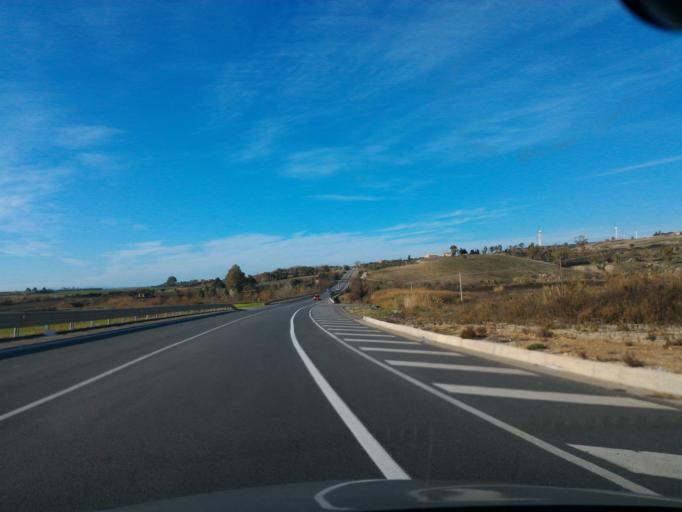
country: IT
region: Calabria
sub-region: Provincia di Crotone
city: Isola di Capo Rizzuto
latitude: 38.9402
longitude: 17.0762
